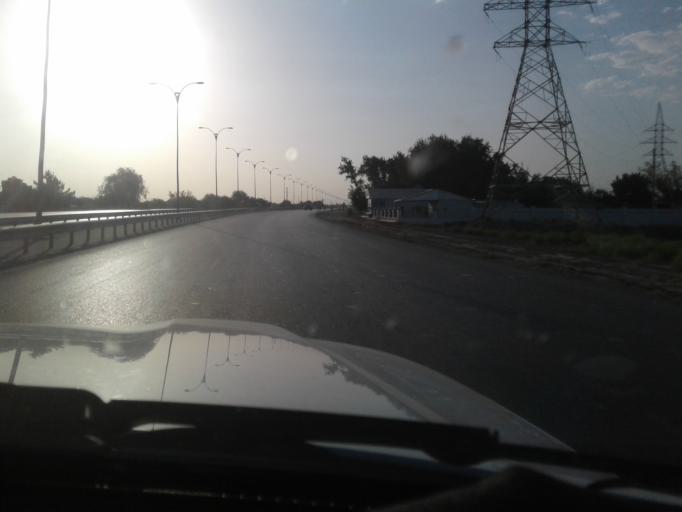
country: TM
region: Mary
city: Mary
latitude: 37.5363
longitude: 61.8844
